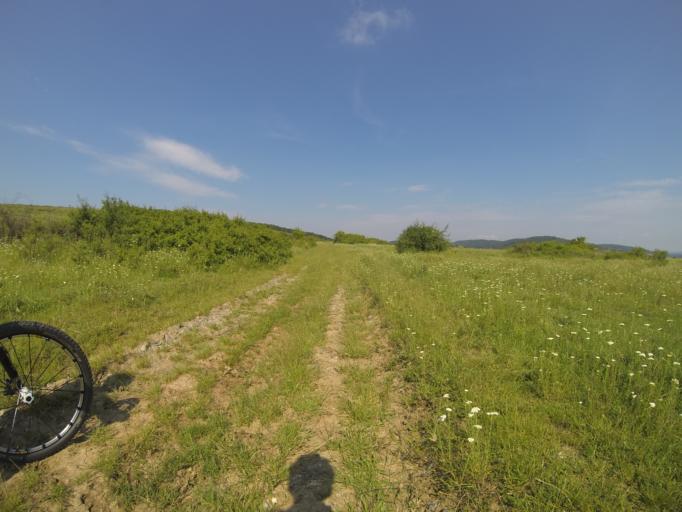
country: RO
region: Gorj
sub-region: Comuna Crusetu
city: Crusetu
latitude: 44.6122
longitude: 23.6679
